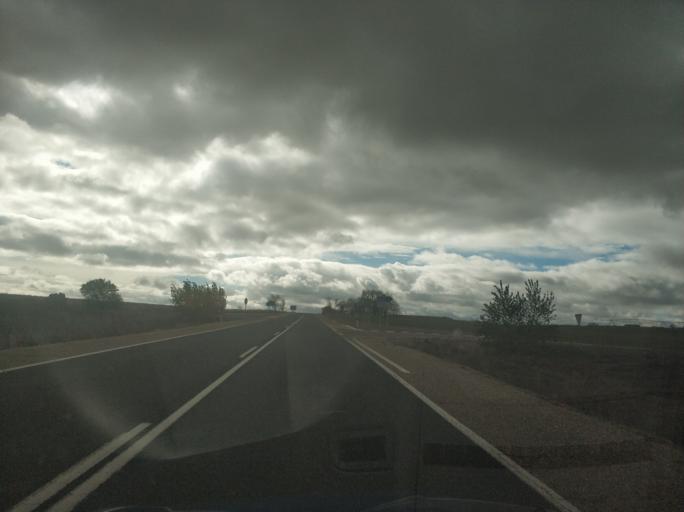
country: ES
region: Castille and Leon
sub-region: Provincia de Zamora
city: Castrillo de la Guarena
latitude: 41.2249
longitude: -5.3139
